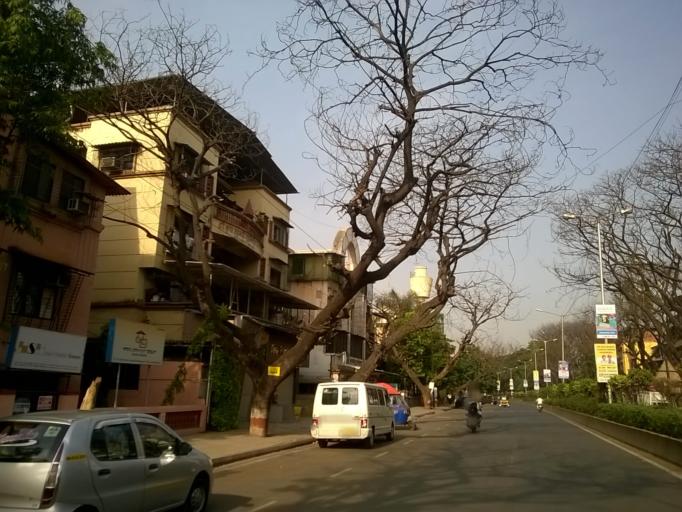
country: IN
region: Maharashtra
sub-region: Raigarh
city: Panvel
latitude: 18.9979
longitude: 73.1220
